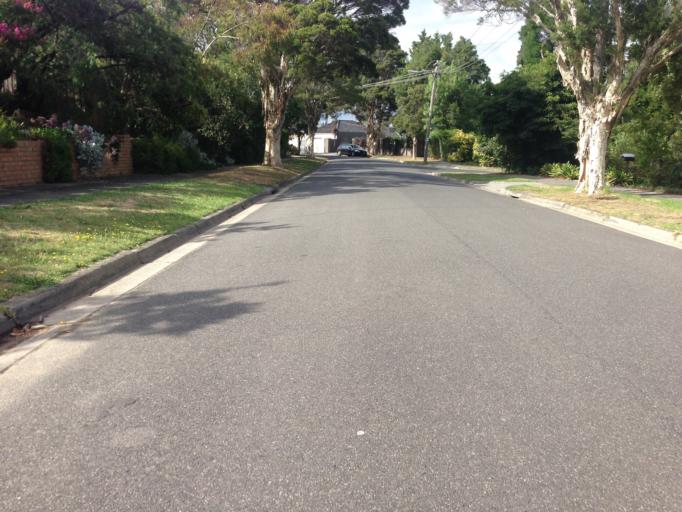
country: AU
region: Victoria
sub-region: Boroondara
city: Balwyn North
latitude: -37.7981
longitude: 145.0856
